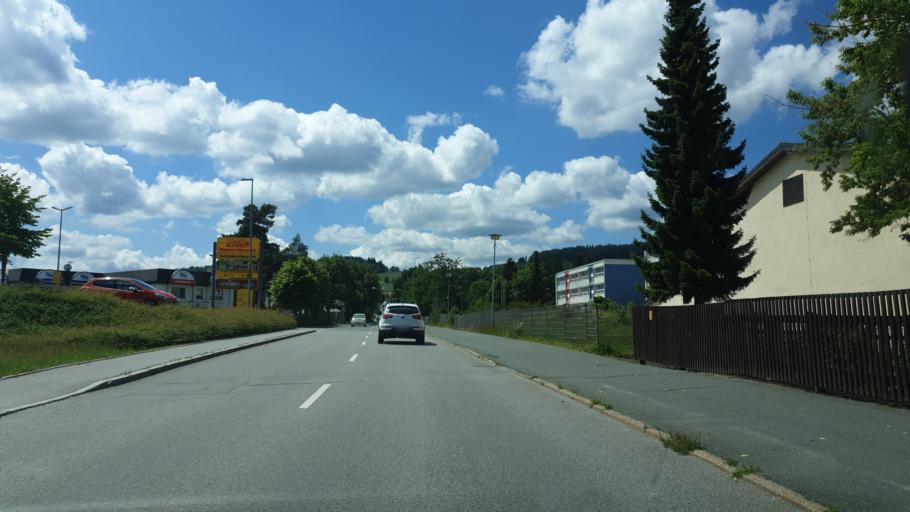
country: DE
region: Saxony
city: Schwarzenberg
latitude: 50.5353
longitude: 12.7731
